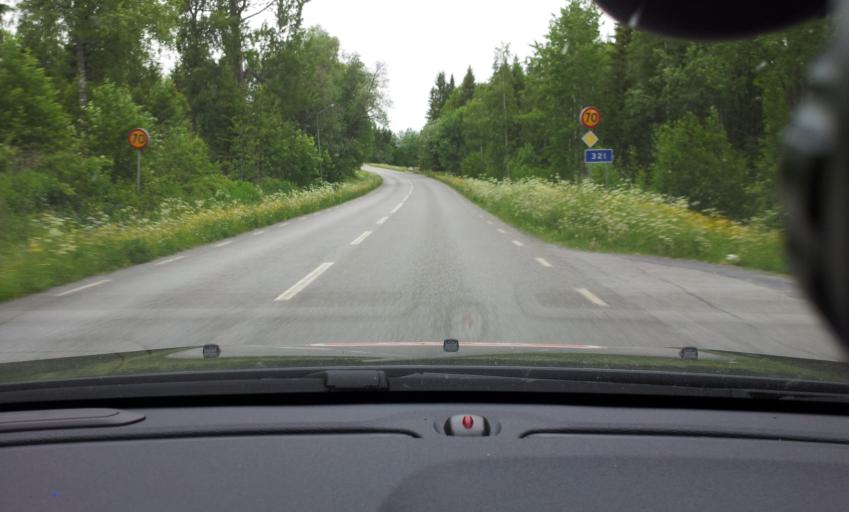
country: SE
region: Jaemtland
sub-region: Krokoms Kommun
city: Krokom
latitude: 63.1797
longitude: 14.0874
